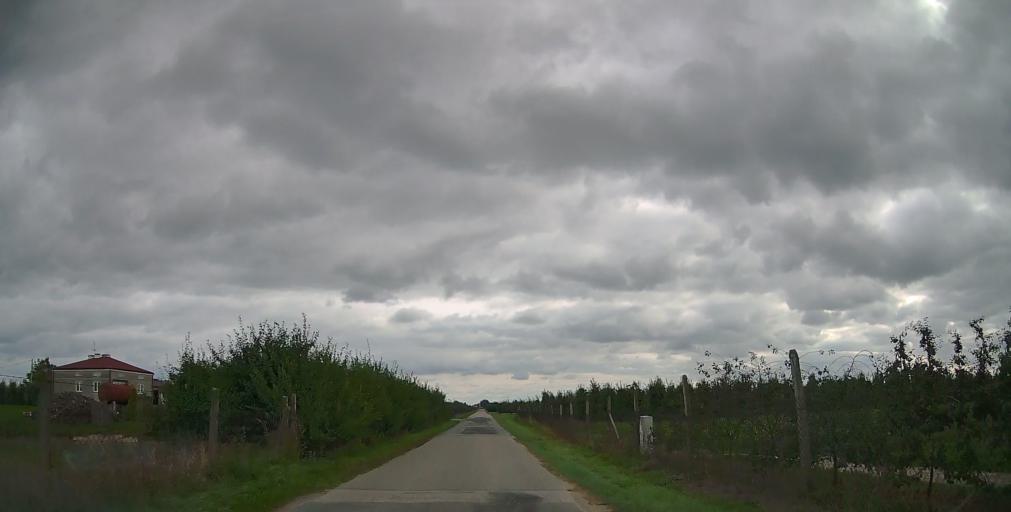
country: PL
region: Masovian Voivodeship
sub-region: Powiat grojecki
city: Goszczyn
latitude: 51.7710
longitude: 20.8657
